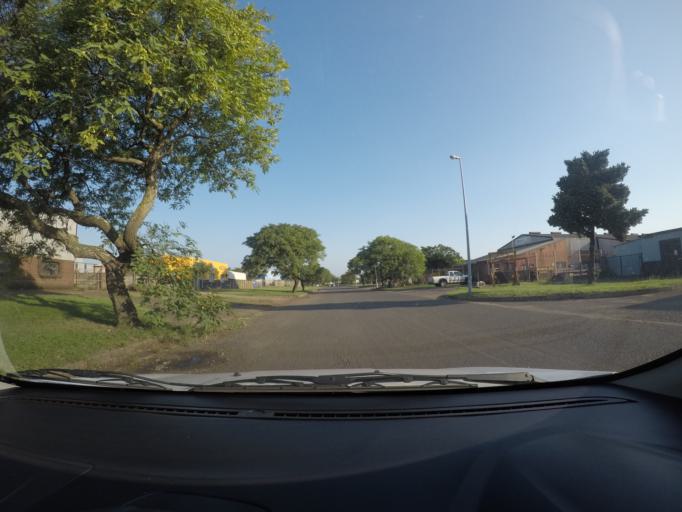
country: ZA
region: KwaZulu-Natal
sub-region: uThungulu District Municipality
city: Richards Bay
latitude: -28.7644
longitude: 32.0047
